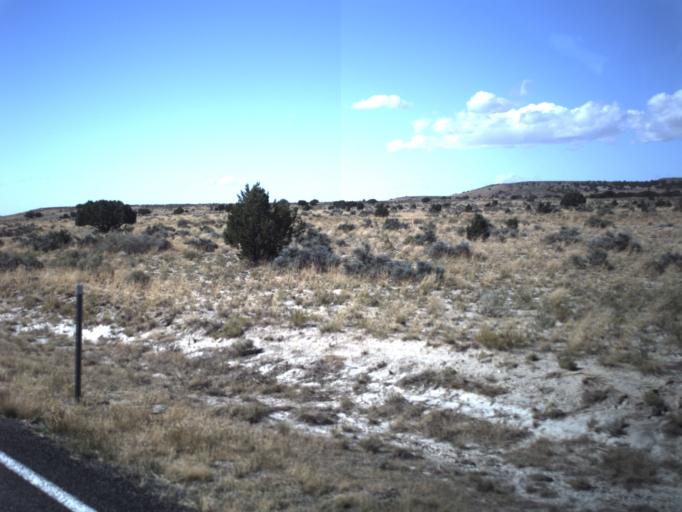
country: US
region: Utah
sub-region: Beaver County
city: Milford
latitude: 38.8355
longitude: -112.8474
